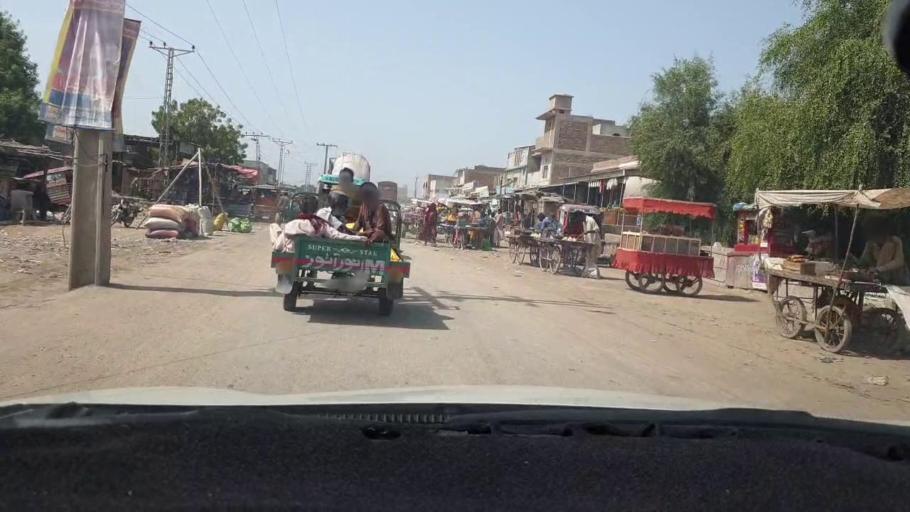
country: PK
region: Sindh
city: Mirpur Khas
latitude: 25.5371
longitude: 69.0289
